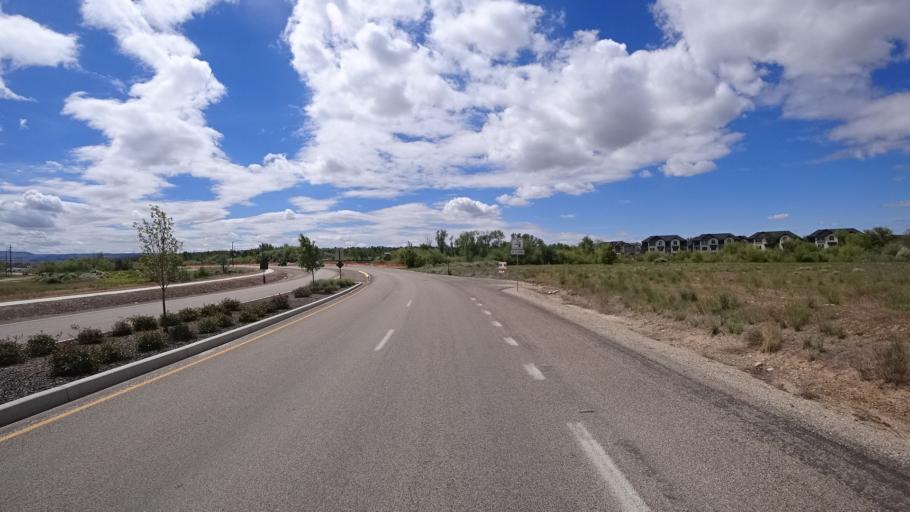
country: US
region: Idaho
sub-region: Ada County
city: Boise
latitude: 43.5754
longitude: -116.1404
